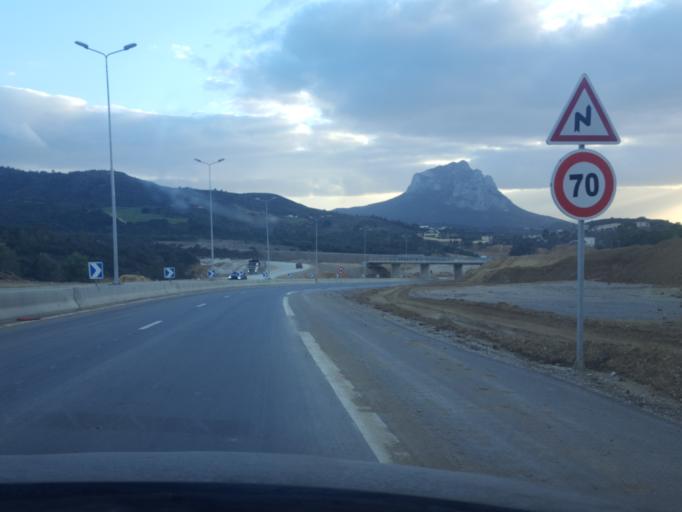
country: TN
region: Tunis
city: La Sebala du Mornag
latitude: 36.6502
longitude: 10.3688
